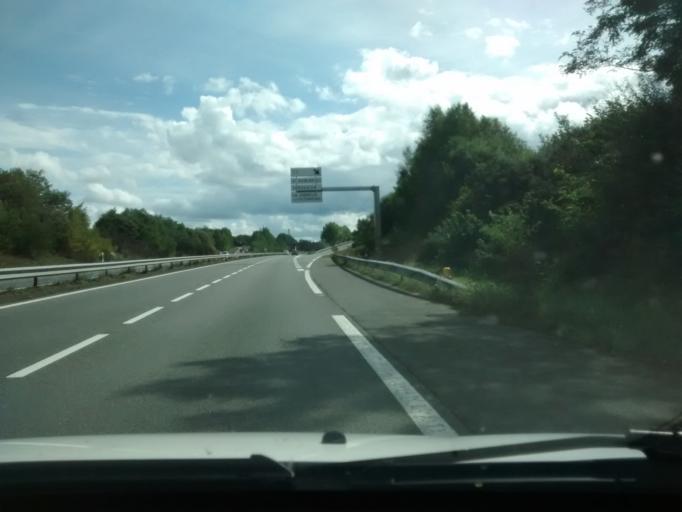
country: FR
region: Brittany
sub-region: Departement d'Ille-et-Vilaine
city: Saint-Domineuc
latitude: 48.3670
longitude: -1.8802
